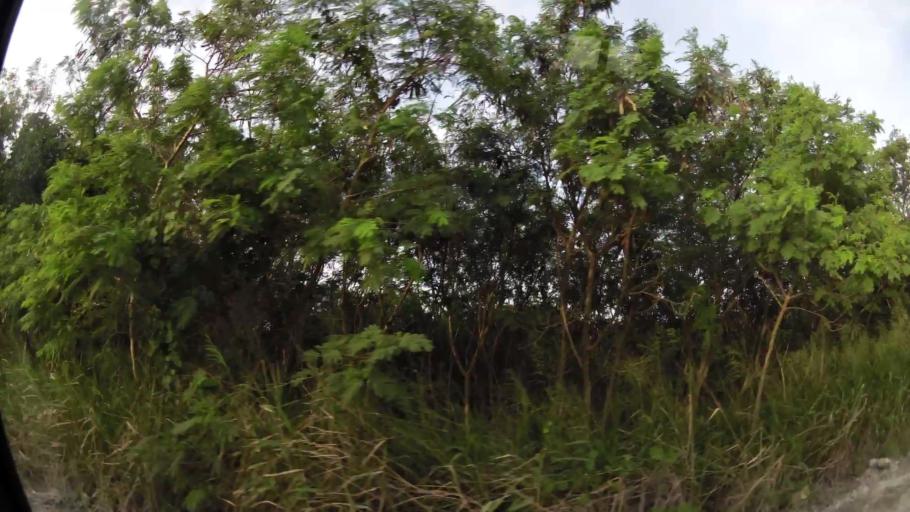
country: BB
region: Christ Church
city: Oistins
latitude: 13.0878
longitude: -59.4979
